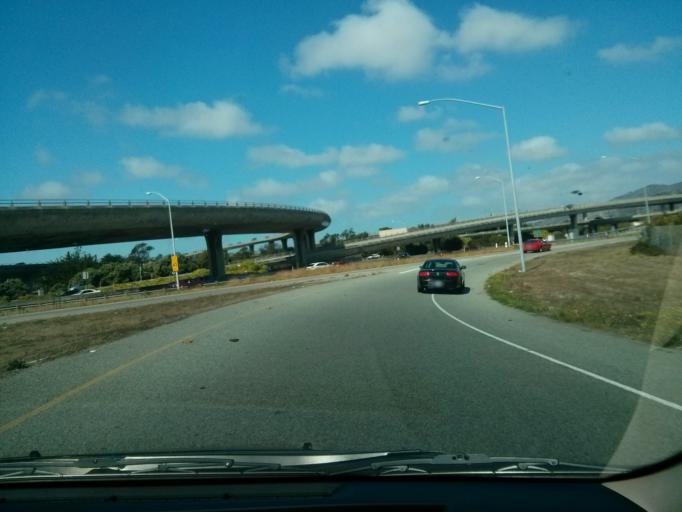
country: US
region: California
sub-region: San Mateo County
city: San Bruno
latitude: 37.6330
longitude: -122.4020
